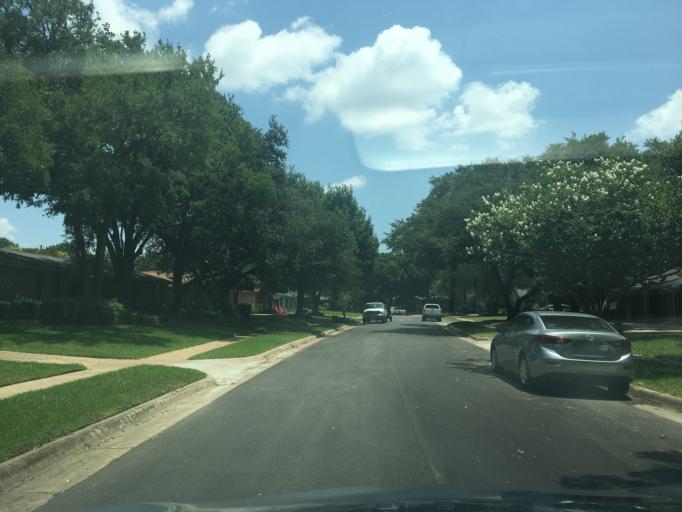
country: US
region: Texas
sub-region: Dallas County
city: Addison
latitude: 32.9147
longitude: -96.8457
